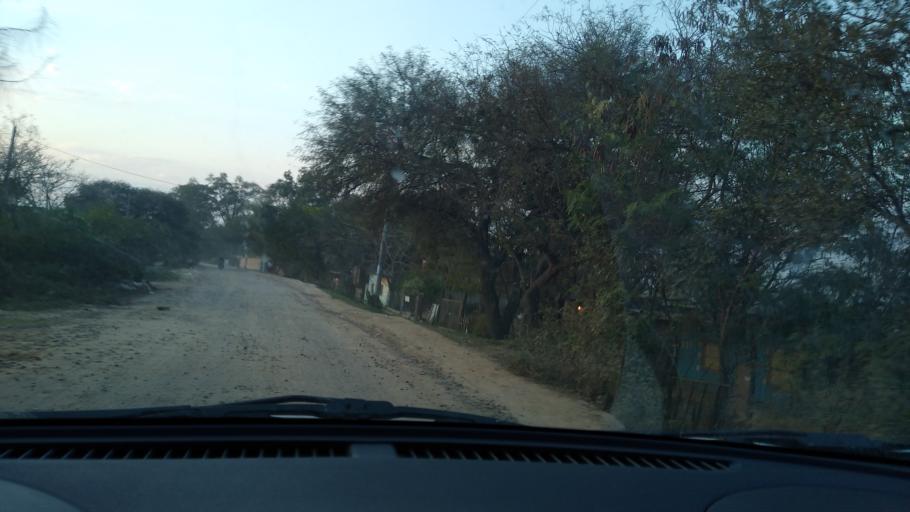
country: AR
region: Chaco
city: Resistencia
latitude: -27.4609
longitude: -58.9592
